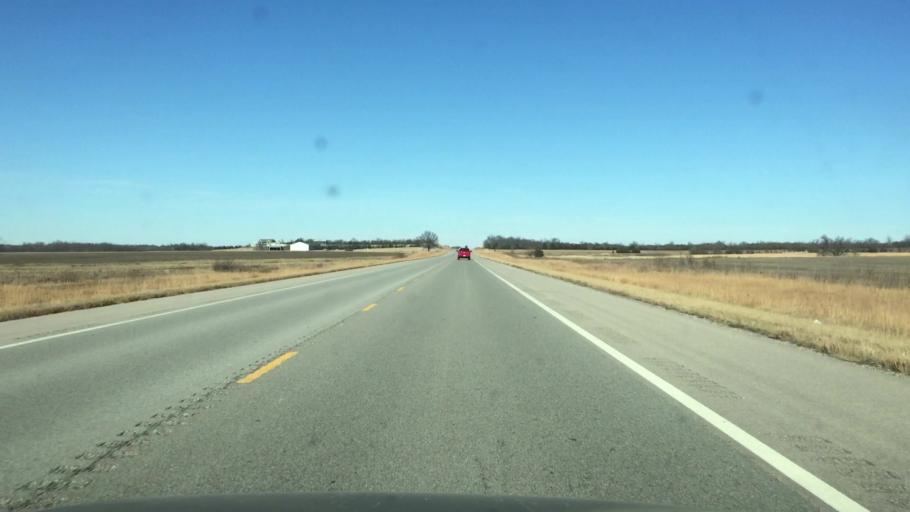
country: US
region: Kansas
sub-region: Allen County
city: Iola
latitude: 37.9605
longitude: -95.3812
